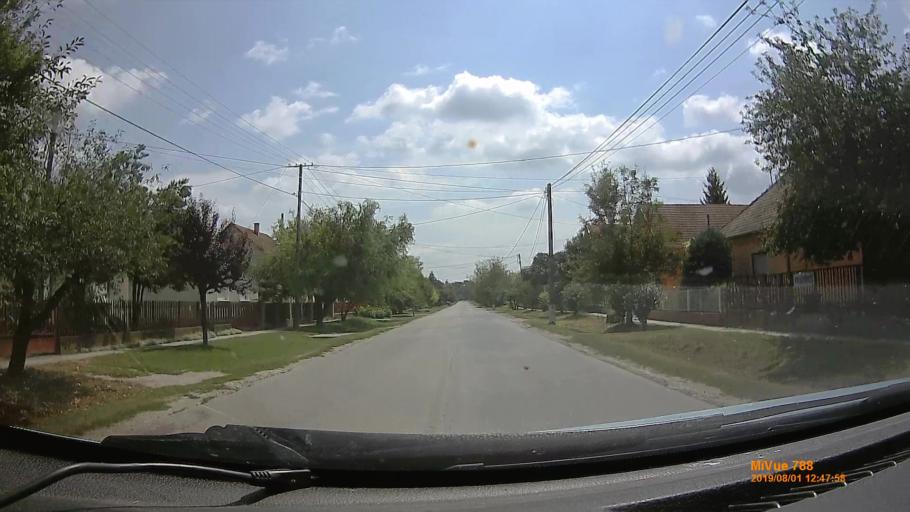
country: HR
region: Osjecko-Baranjska
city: Viljevo
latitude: 45.8216
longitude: 18.1037
